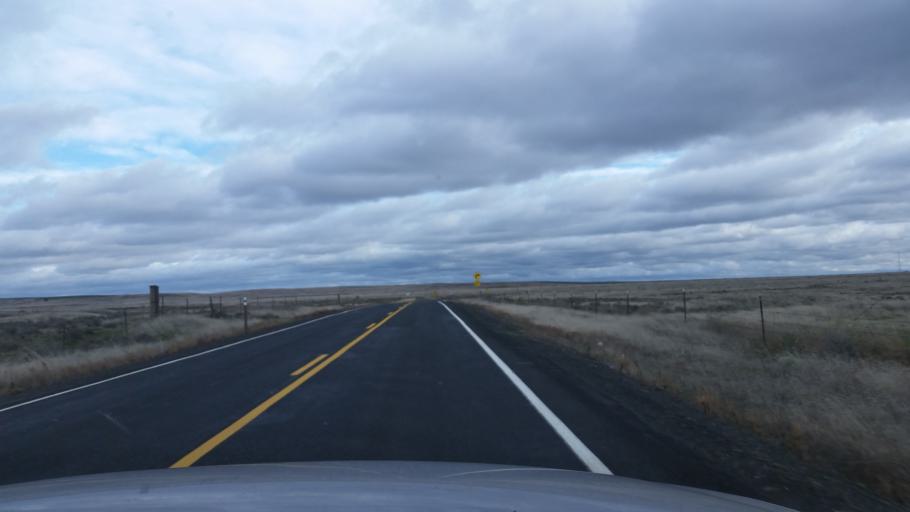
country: US
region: Washington
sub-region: Lincoln County
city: Davenport
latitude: 47.3340
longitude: -117.9875
